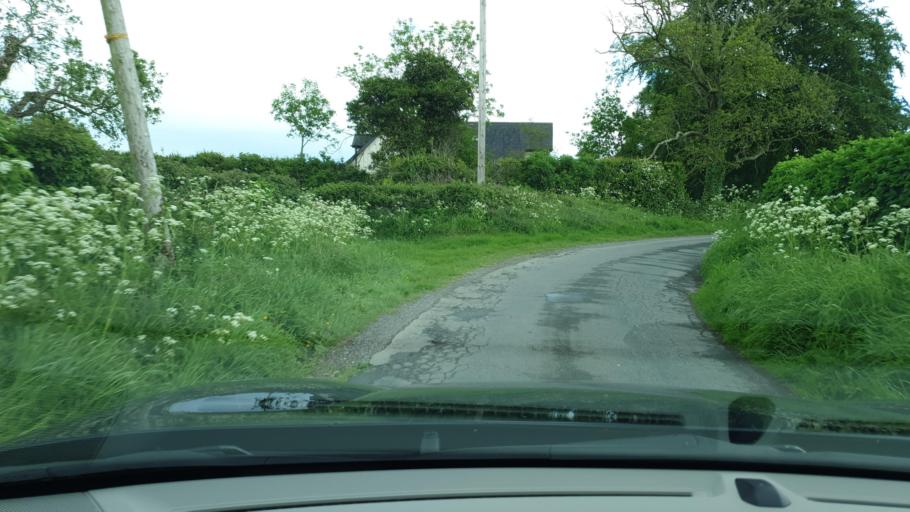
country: IE
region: Leinster
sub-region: An Mhi
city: Ratoath
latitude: 53.5262
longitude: -6.4547
